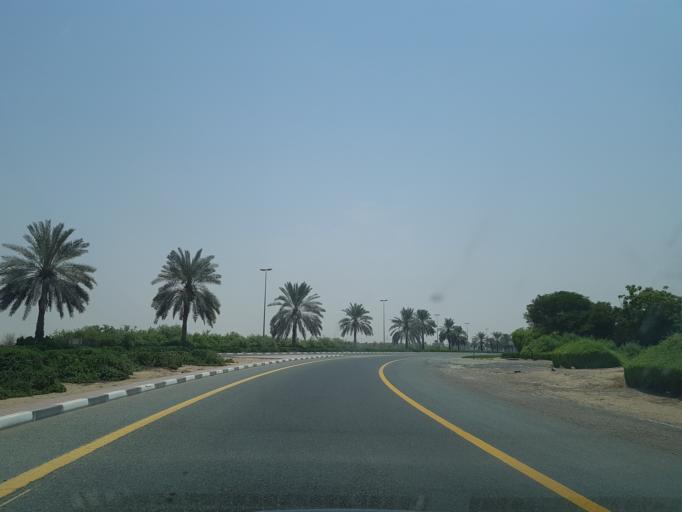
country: AE
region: Ash Shariqah
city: Sharjah
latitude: 25.1129
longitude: 55.3933
